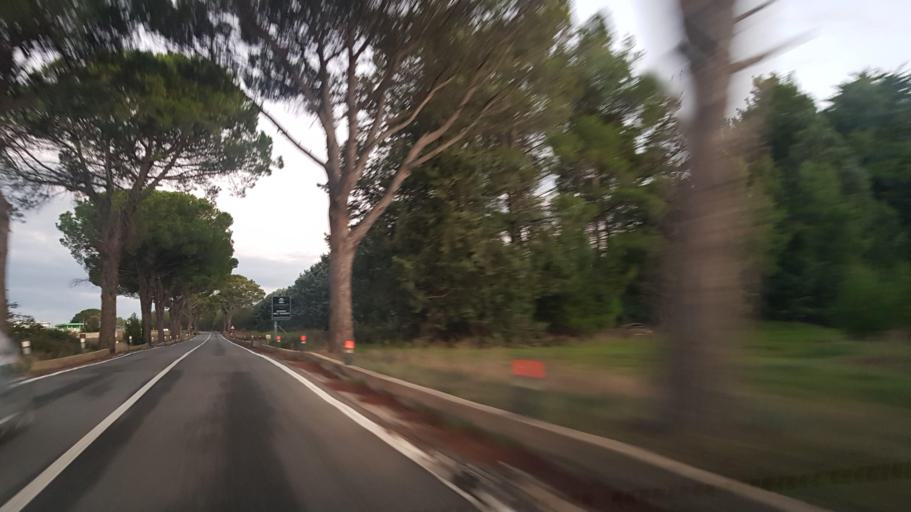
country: IT
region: Basilicate
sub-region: Provincia di Matera
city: Matera
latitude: 40.6792
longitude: 16.6503
